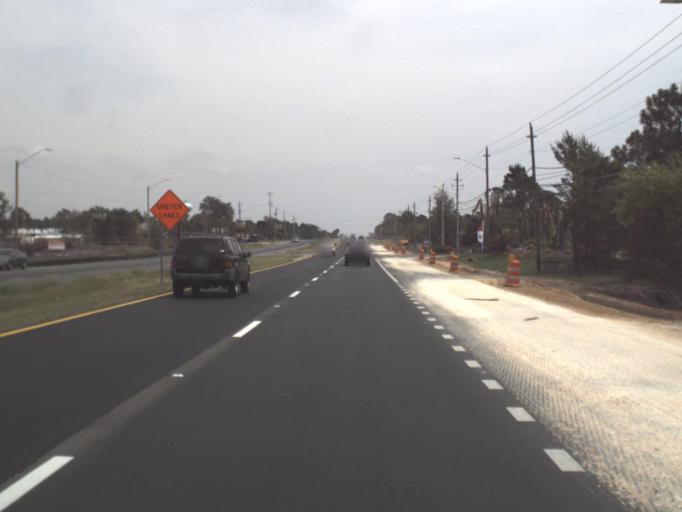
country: US
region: Florida
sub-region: Santa Rosa County
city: Holley
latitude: 30.4021
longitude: -86.9335
